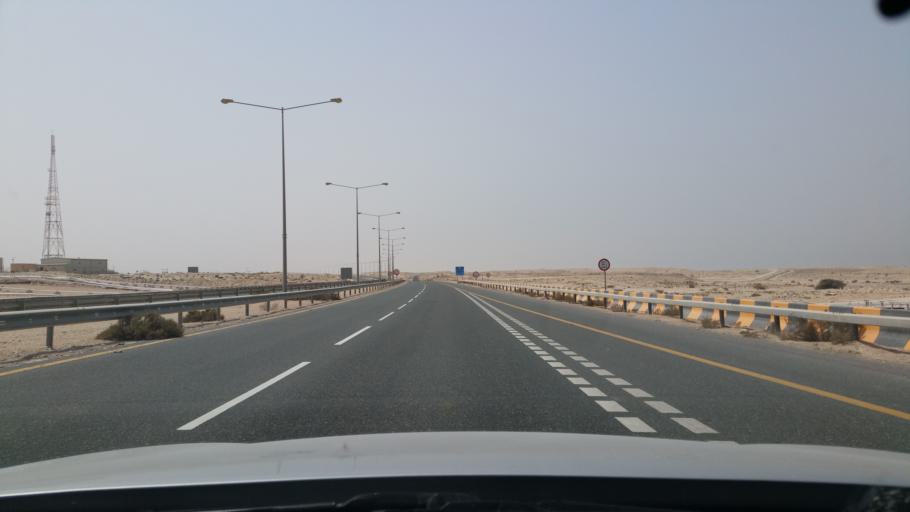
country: QA
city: Umm Bab
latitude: 25.2907
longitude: 50.7907
